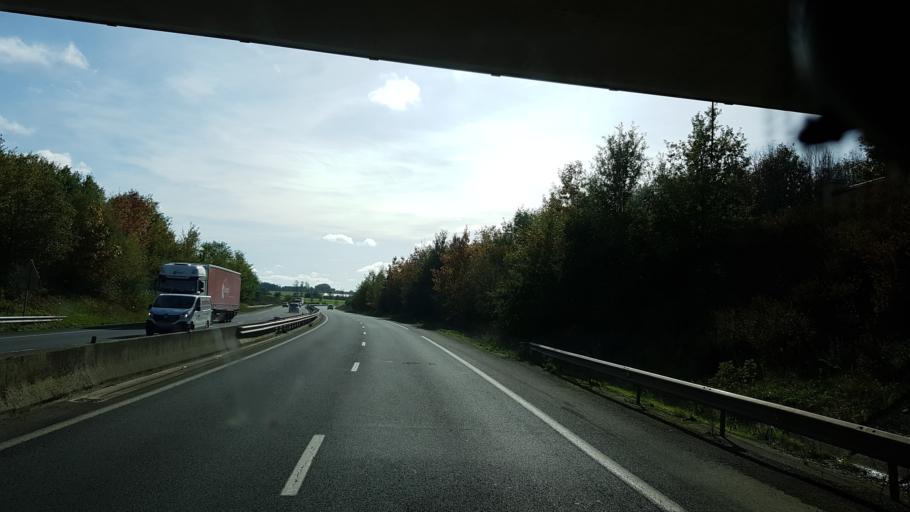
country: FR
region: Poitou-Charentes
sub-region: Departement de la Charente
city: Chasseneuil-sur-Bonnieure
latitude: 45.8228
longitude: 0.4574
